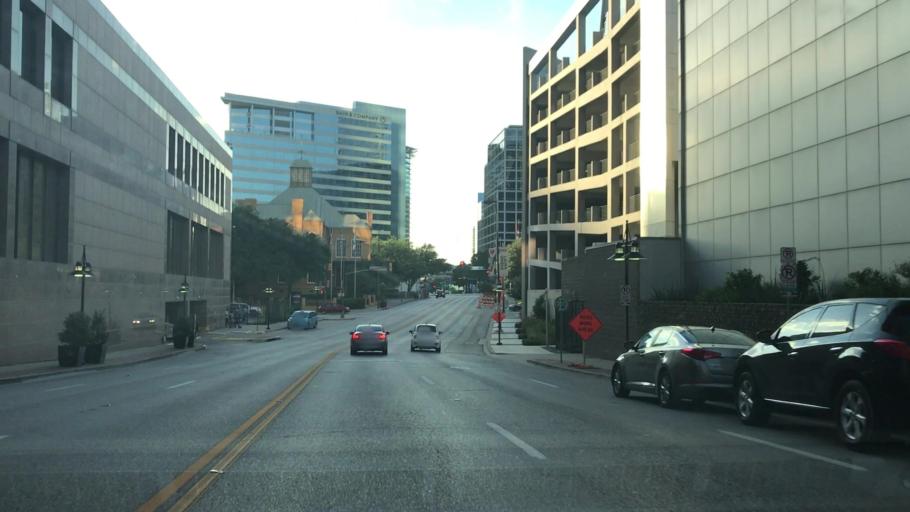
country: US
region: Texas
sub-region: Dallas County
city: Dallas
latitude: 32.7861
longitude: -96.8016
